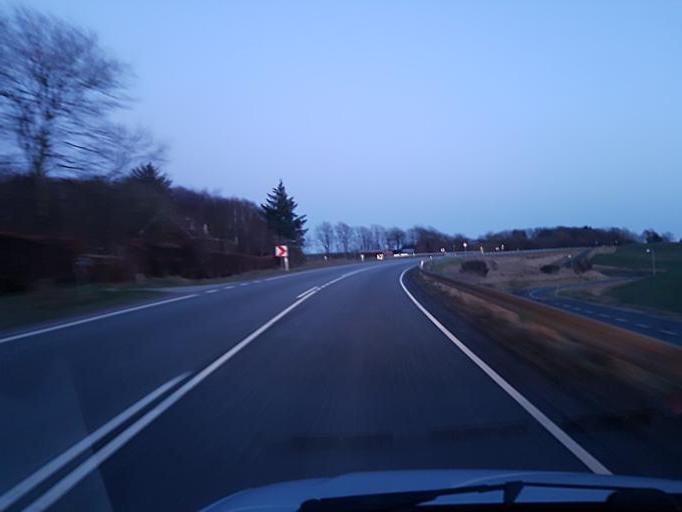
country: DK
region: Central Jutland
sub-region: Ringkobing-Skjern Kommune
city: Videbaek
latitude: 56.1078
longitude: 8.5070
